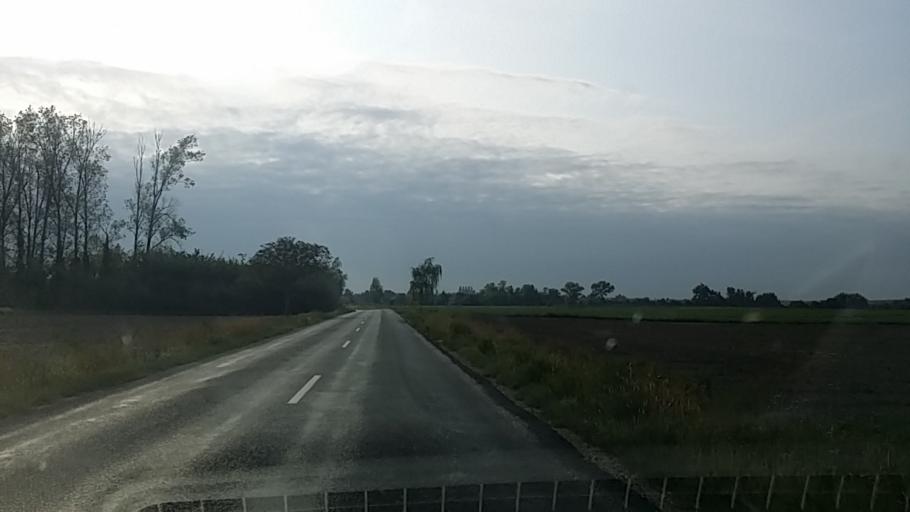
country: HU
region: Gyor-Moson-Sopron
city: Fertod
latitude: 47.6105
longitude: 16.8967
